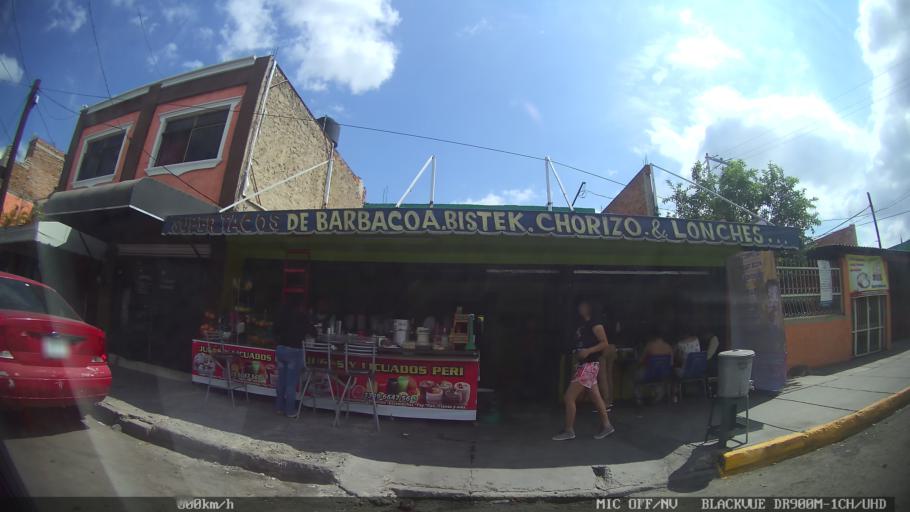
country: MX
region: Jalisco
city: Tonala
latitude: 20.6298
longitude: -103.2473
